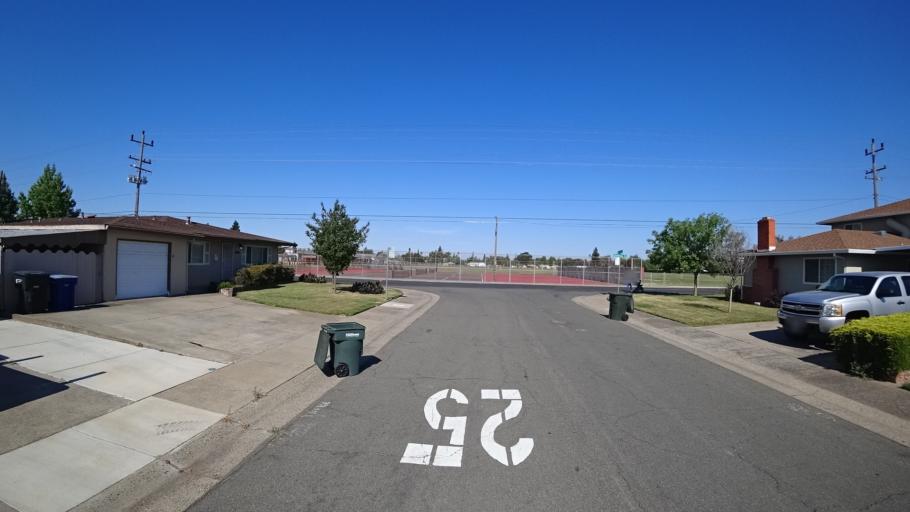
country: US
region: California
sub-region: Sacramento County
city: Florin
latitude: 38.5423
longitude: -121.4228
